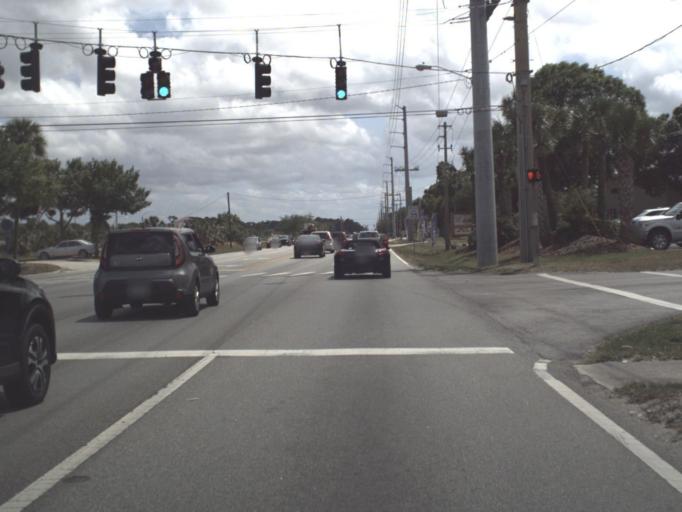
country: US
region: Florida
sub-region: Brevard County
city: June Park
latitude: 28.1186
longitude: -80.6727
